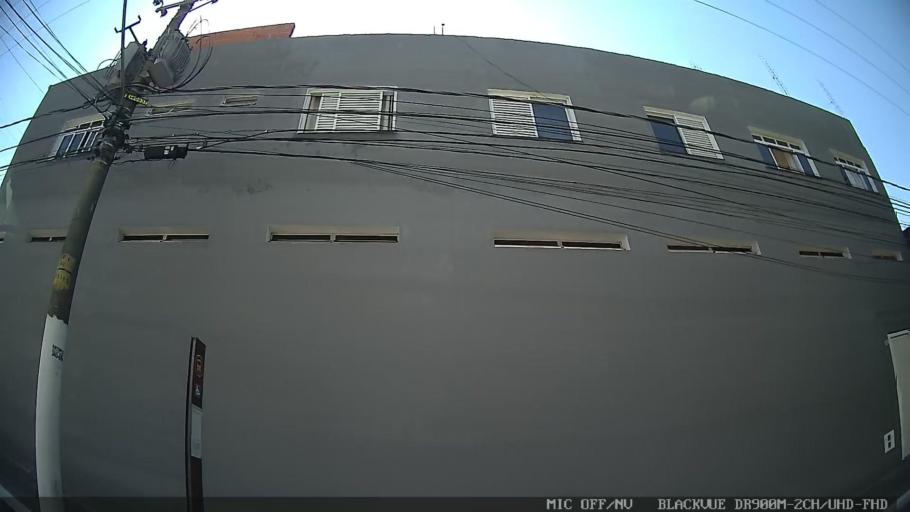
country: BR
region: Sao Paulo
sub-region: Sao Caetano Do Sul
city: Sao Caetano do Sul
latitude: -23.6058
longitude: -46.4876
